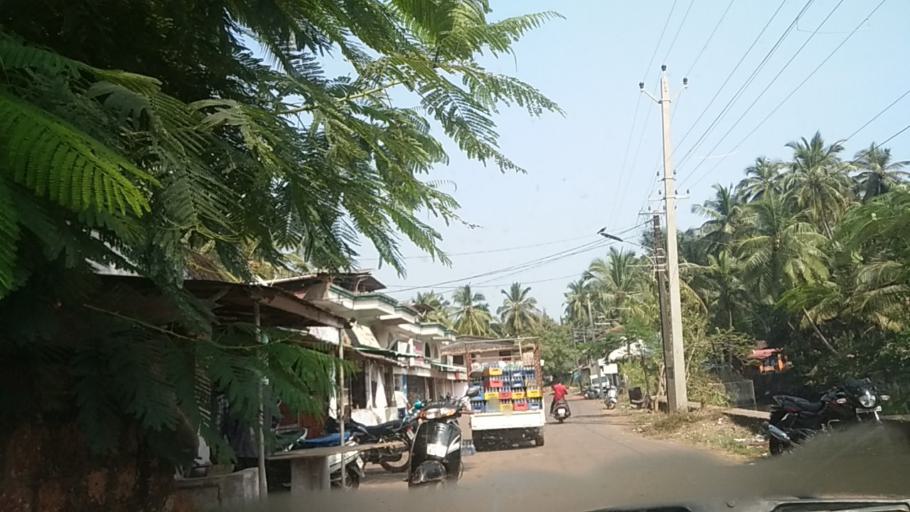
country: IN
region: Goa
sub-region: South Goa
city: Cavelossim
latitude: 15.1466
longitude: 73.9555
